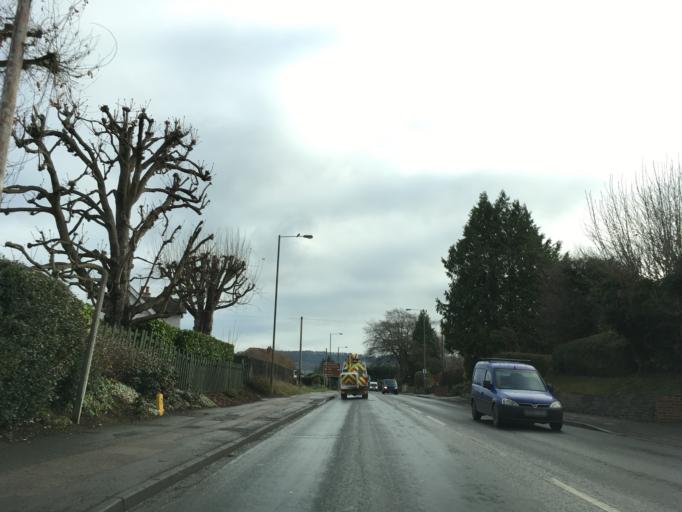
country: GB
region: England
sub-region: Gloucestershire
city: Churchdown
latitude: 51.8440
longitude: -2.1536
